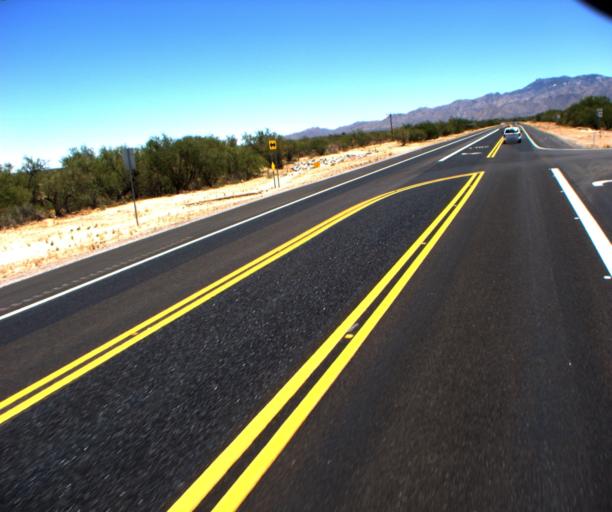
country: US
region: Arizona
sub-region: Pima County
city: Sells
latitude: 31.9276
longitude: -111.7937
